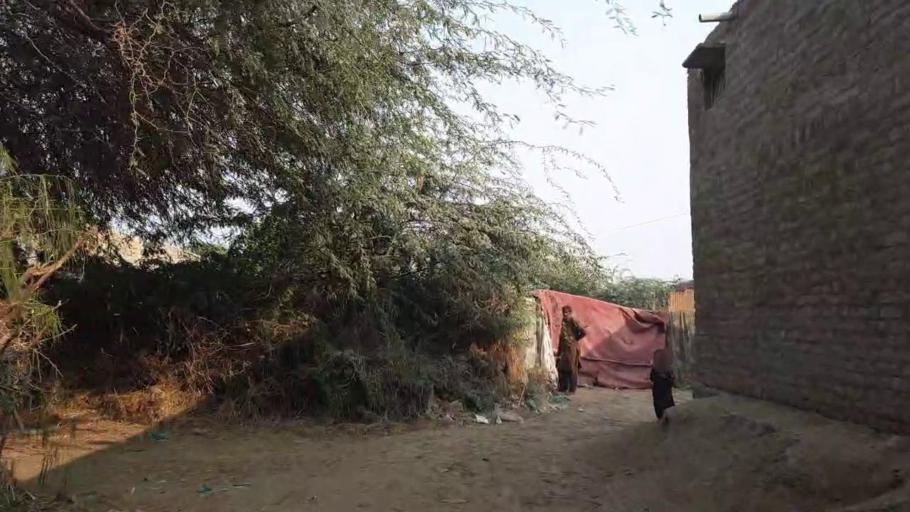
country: PK
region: Sindh
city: Tando Muhammad Khan
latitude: 25.1432
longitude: 68.6149
